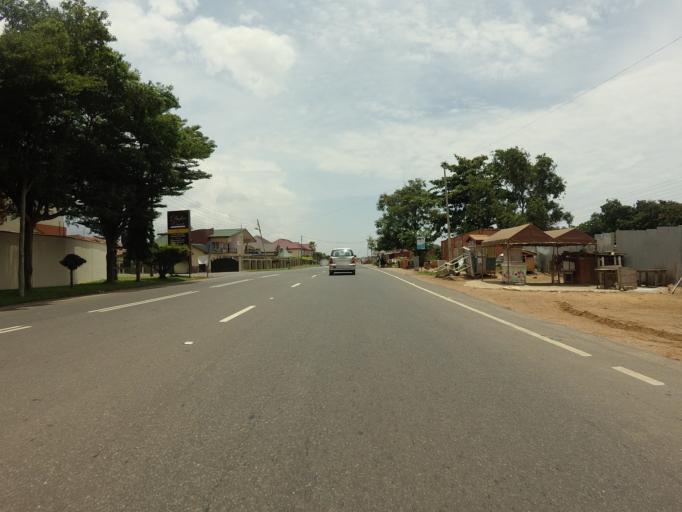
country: GH
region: Greater Accra
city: Medina Estates
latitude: 5.6345
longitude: -0.1470
